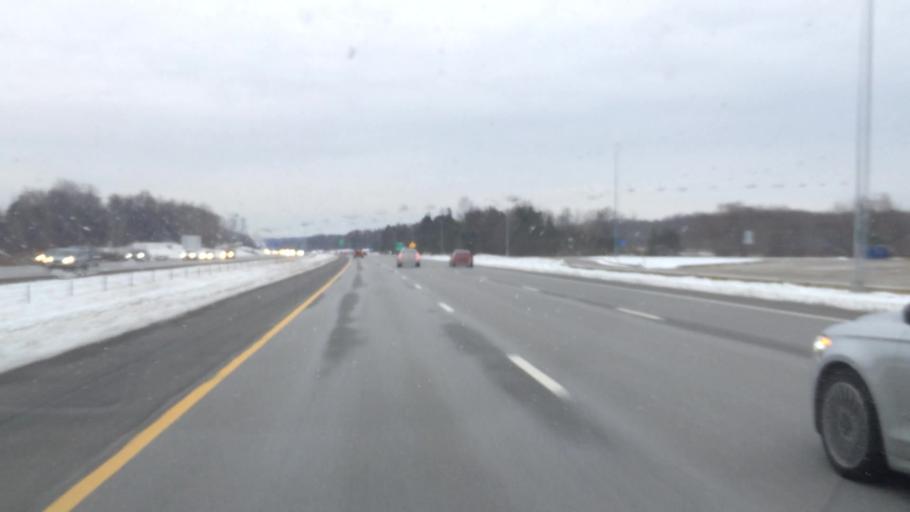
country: US
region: Ohio
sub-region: Medina County
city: Brunswick
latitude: 41.2102
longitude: -81.7937
